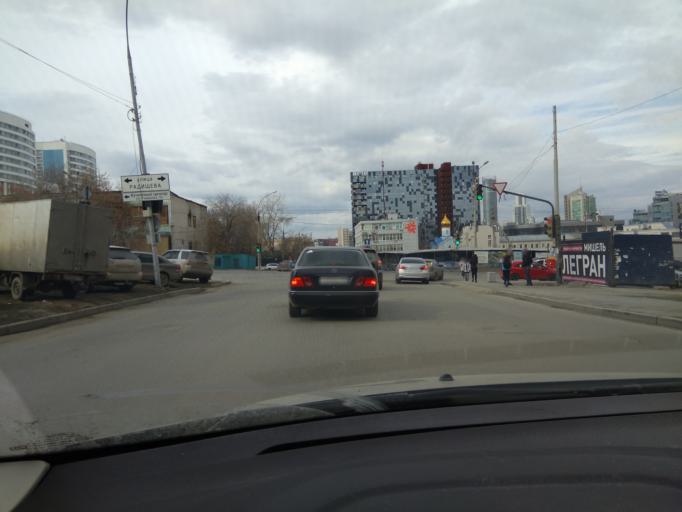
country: RU
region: Sverdlovsk
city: Yekaterinburg
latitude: 56.8290
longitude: 60.5878
